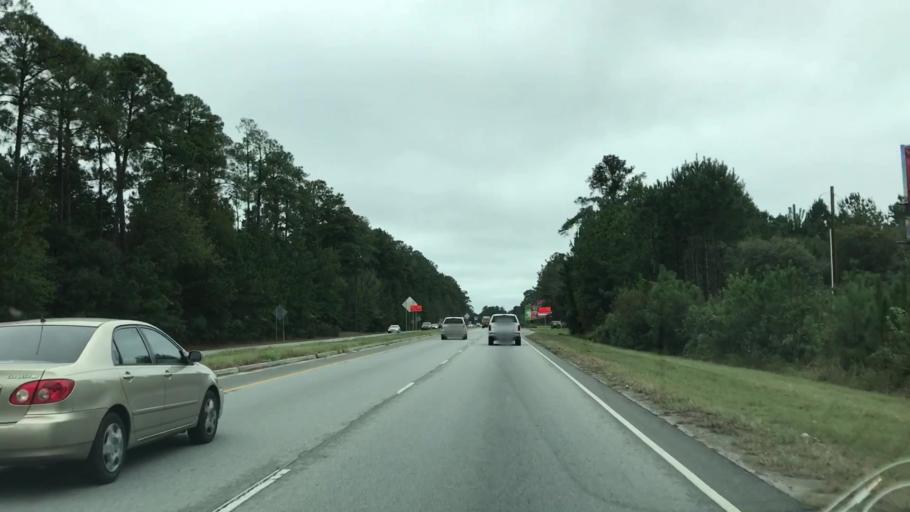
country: US
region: South Carolina
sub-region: Beaufort County
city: Bluffton
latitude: 32.3107
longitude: -80.9349
